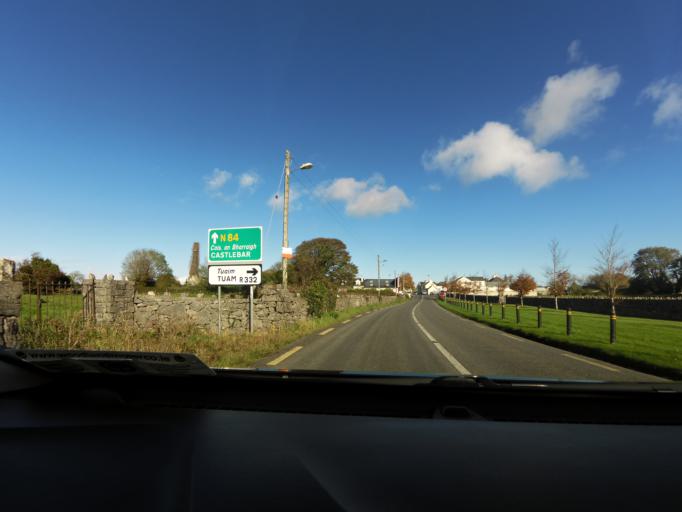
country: IE
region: Connaught
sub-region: Maigh Eo
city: Ballinrobe
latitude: 53.5778
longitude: -9.1224
